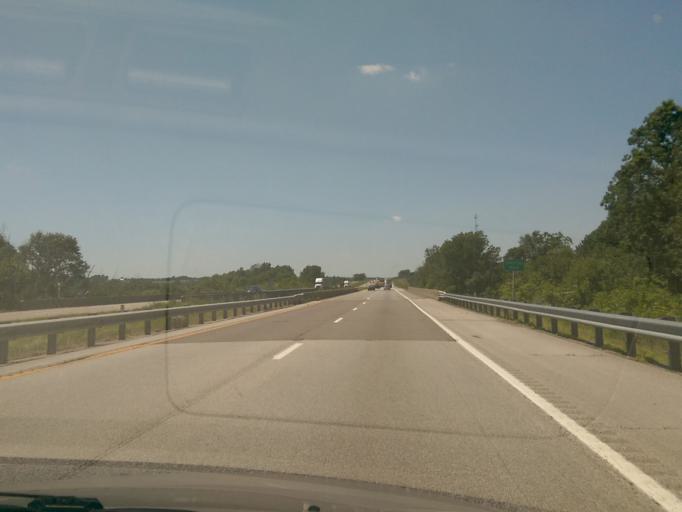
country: US
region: Missouri
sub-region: Cooper County
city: Boonville
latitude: 38.9350
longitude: -92.8995
